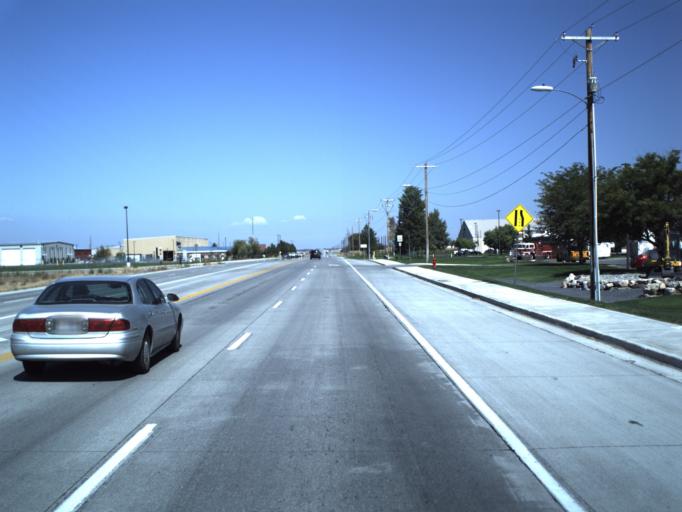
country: US
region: Utah
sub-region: Cache County
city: Logan
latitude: 41.7583
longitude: -111.8587
